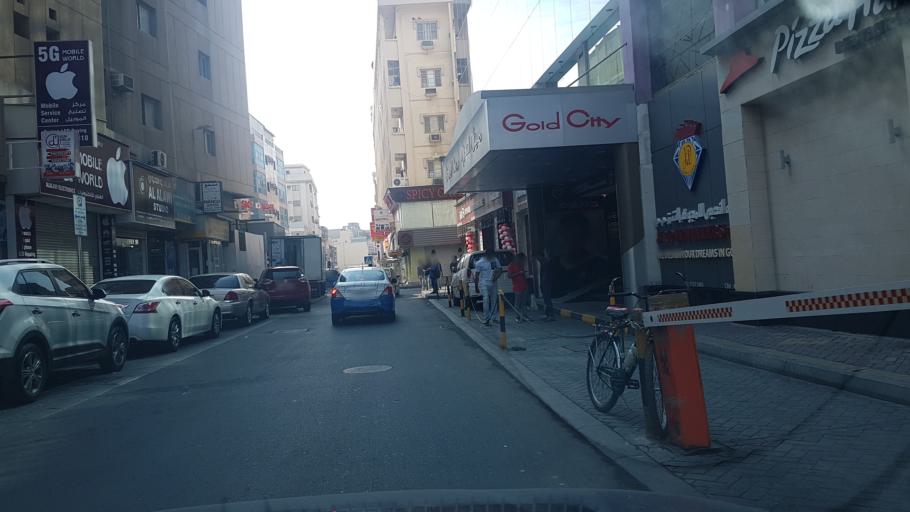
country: BH
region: Manama
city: Manama
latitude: 26.2320
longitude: 50.5736
